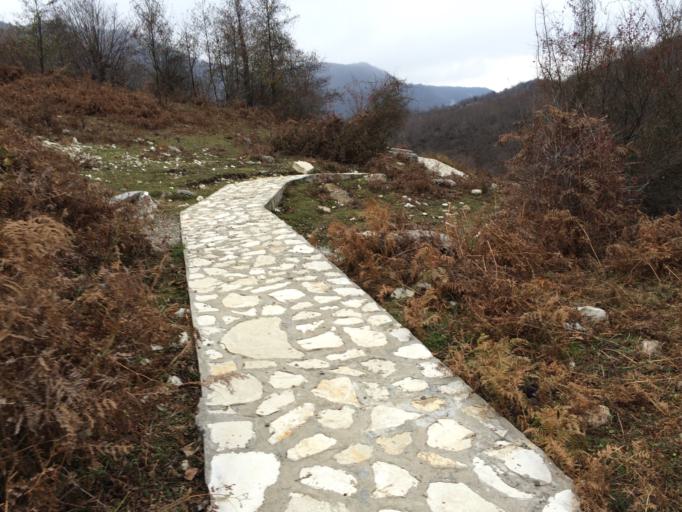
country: GE
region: Imereti
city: Tsqaltubo
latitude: 42.4557
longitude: 42.5466
